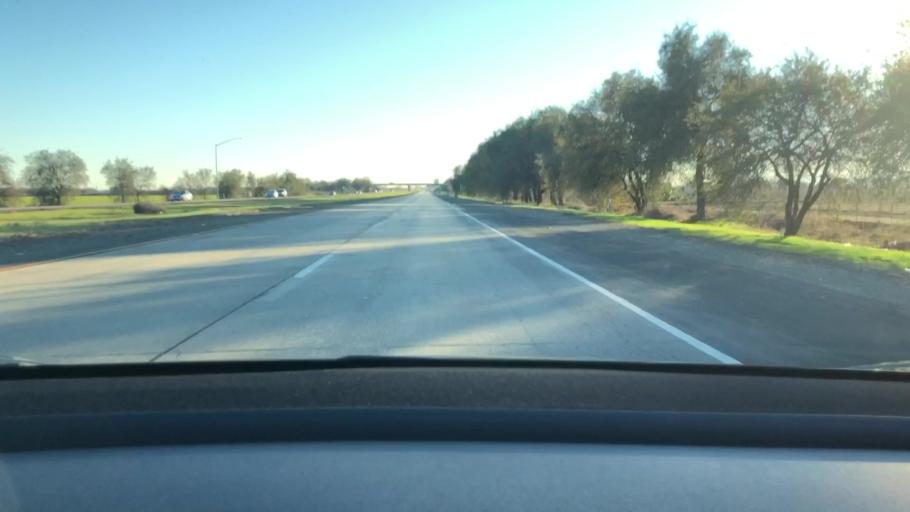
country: US
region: California
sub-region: Yolo County
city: Woodland
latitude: 38.6474
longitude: -121.7574
